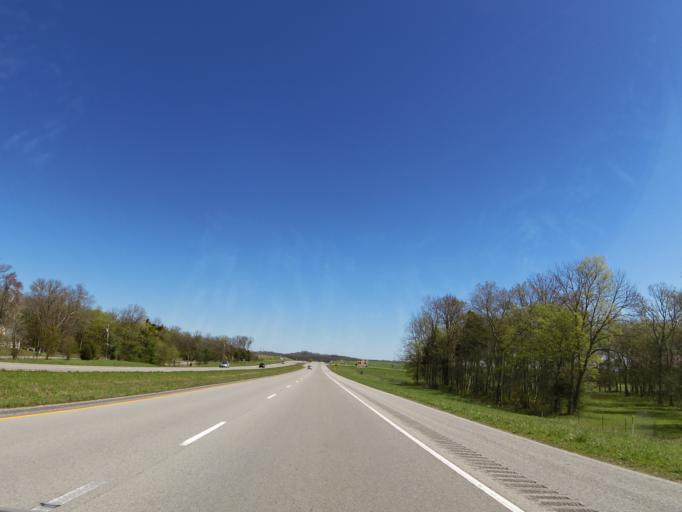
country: US
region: Kentucky
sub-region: Logan County
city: Auburn
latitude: 36.8822
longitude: -86.6644
